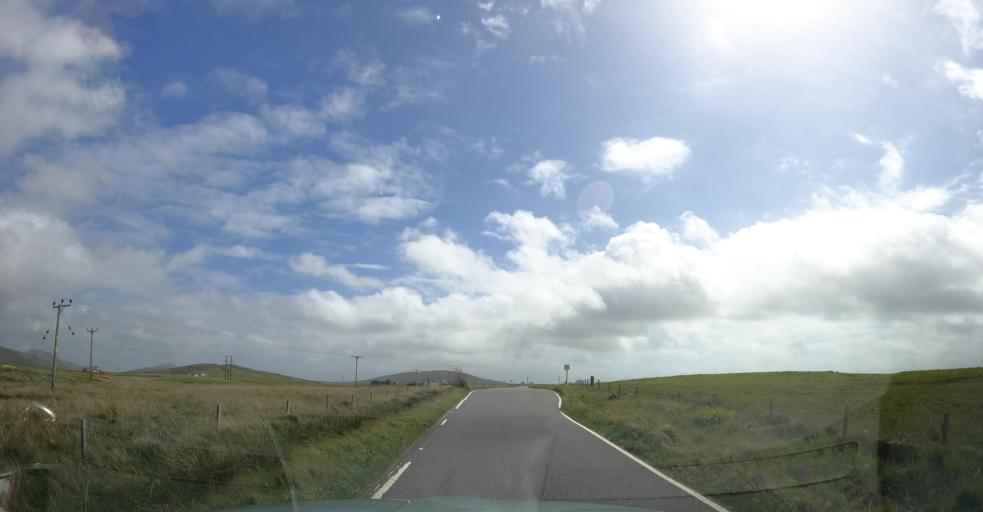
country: GB
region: Scotland
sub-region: Eilean Siar
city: Isle of South Uist
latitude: 57.2148
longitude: -7.3949
